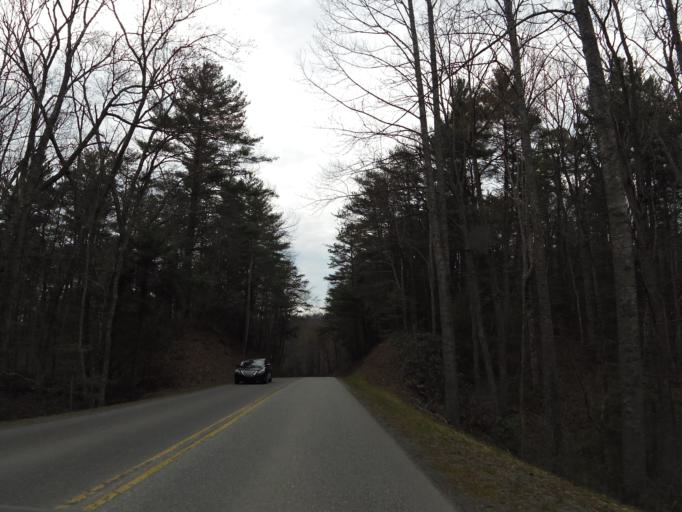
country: US
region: Tennessee
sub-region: Blount County
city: Wildwood
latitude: 35.6034
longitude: -83.7605
